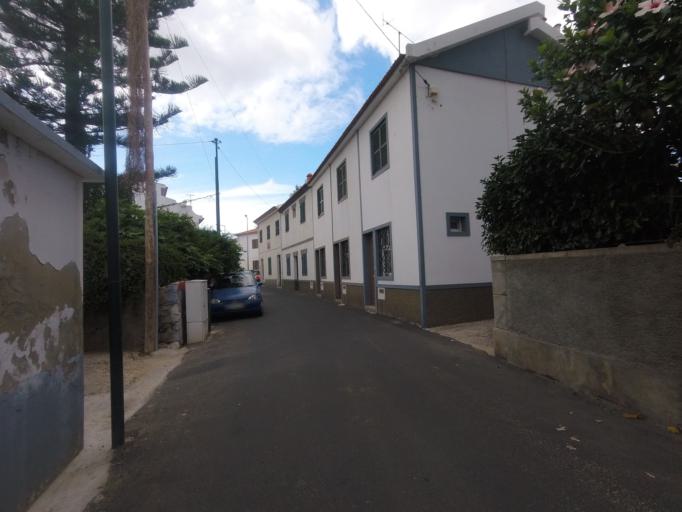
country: PT
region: Madeira
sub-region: Porto Santo
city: Vila de Porto Santo
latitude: 33.0617
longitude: -16.3343
